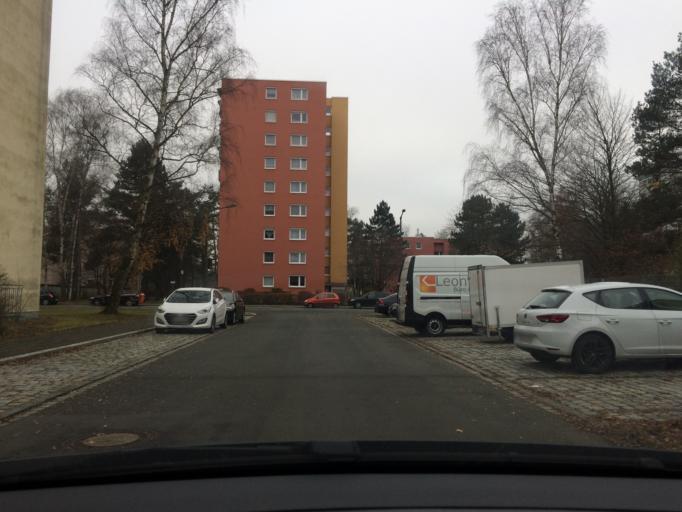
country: DE
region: Bavaria
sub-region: Regierungsbezirk Mittelfranken
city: Nuernberg
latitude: 49.4100
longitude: 11.1212
